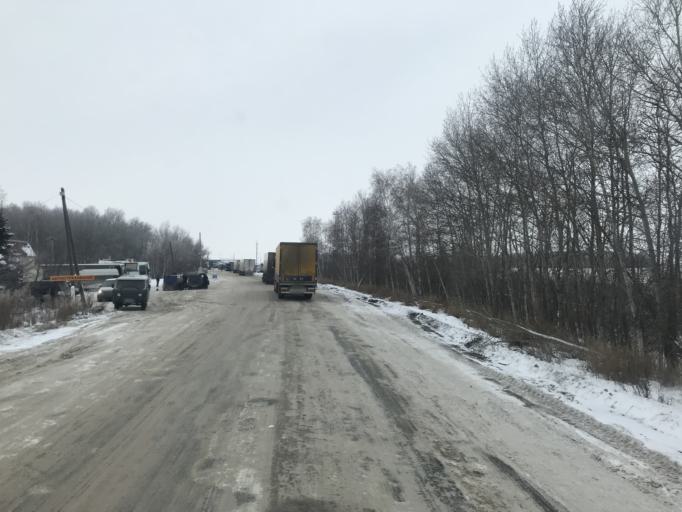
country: RU
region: Kurgan
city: Petukhovo
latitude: 55.0940
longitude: 68.2833
